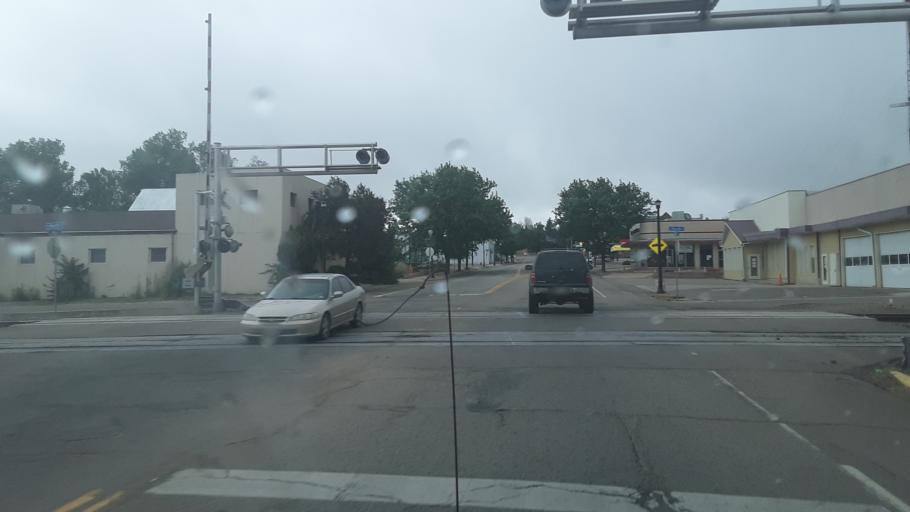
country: US
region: Colorado
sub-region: Huerfano County
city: Walsenburg
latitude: 37.6254
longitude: -104.7817
